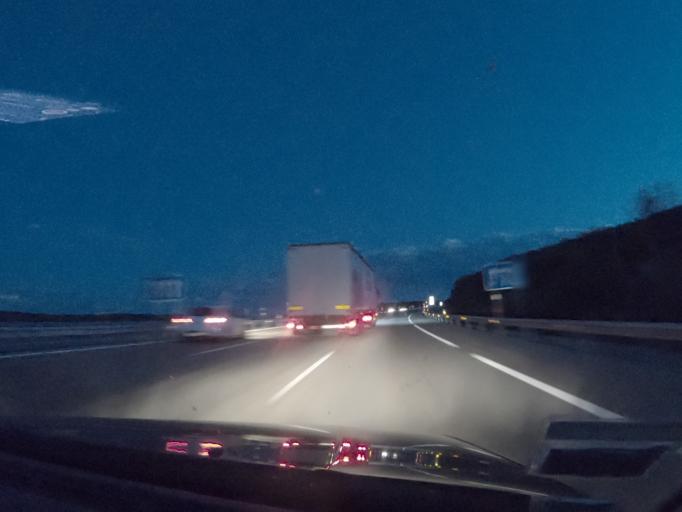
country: ES
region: Castille and Leon
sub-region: Provincia de Leon
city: Villagaton
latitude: 42.5881
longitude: -6.2154
